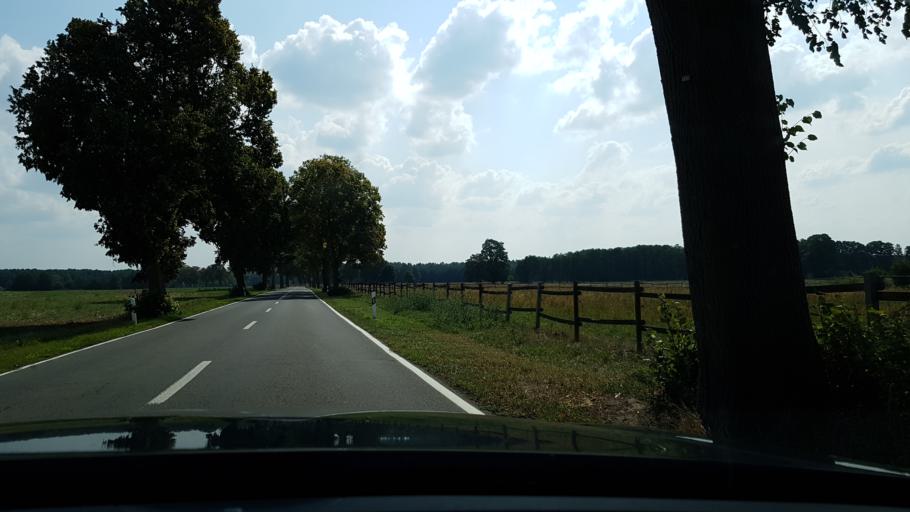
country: DE
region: Brandenburg
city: Lindow
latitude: 53.0209
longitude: 12.9750
